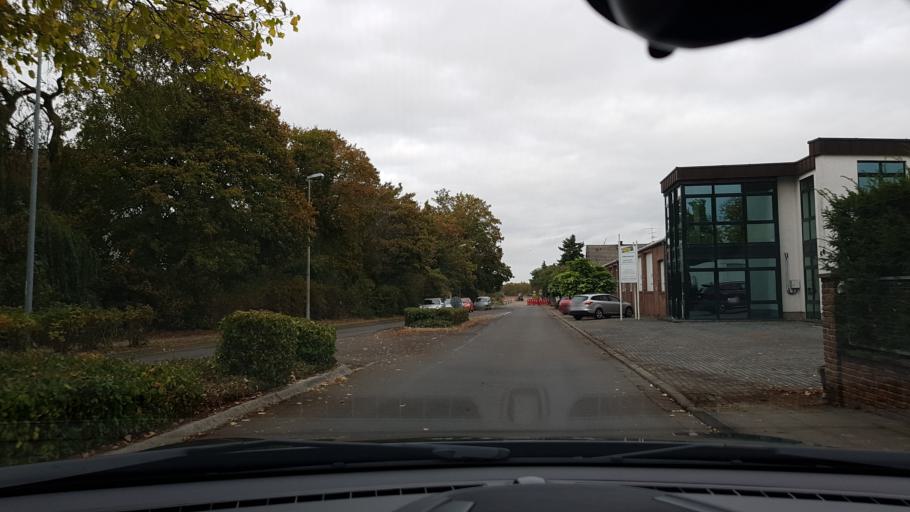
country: DE
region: North Rhine-Westphalia
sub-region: Regierungsbezirk Koln
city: Elsdorf
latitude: 50.9430
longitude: 6.5772
